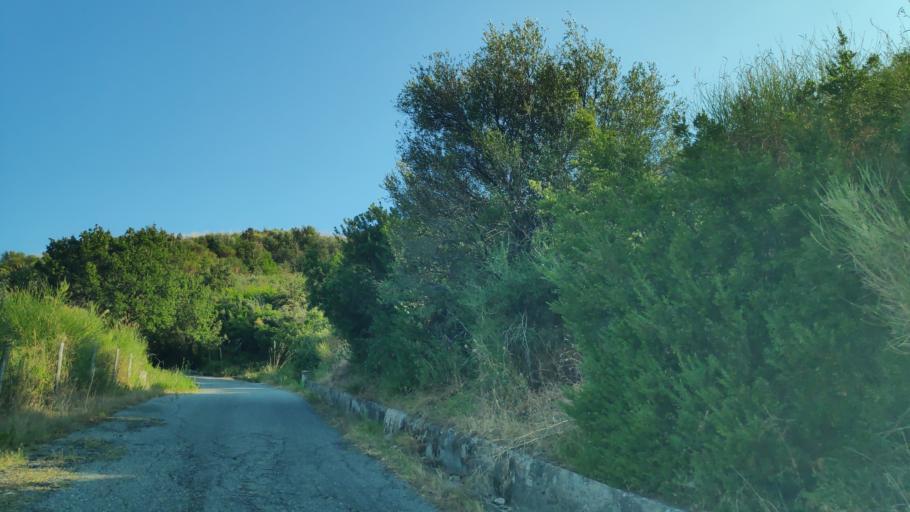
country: IT
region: Calabria
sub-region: Provincia di Reggio Calabria
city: Placanica
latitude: 38.4099
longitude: 16.4357
